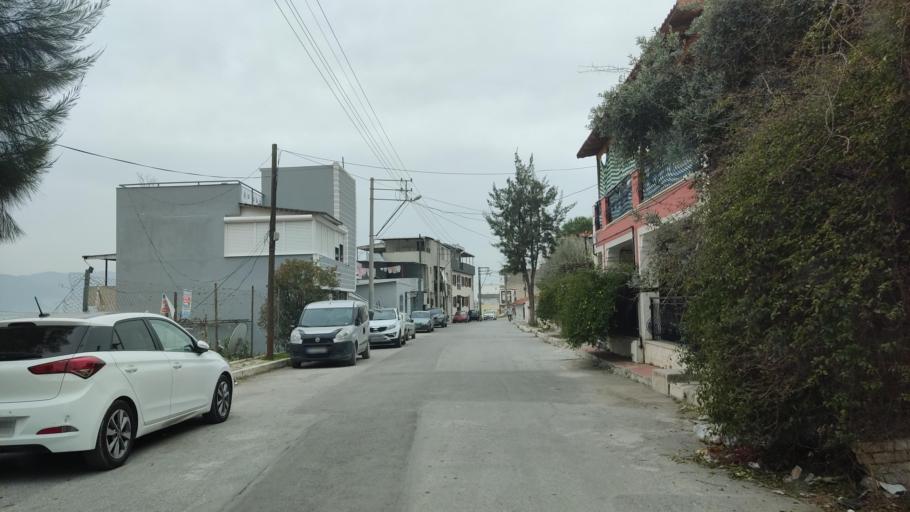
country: TR
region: Izmir
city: Karsiyaka
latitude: 38.4926
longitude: 27.0707
